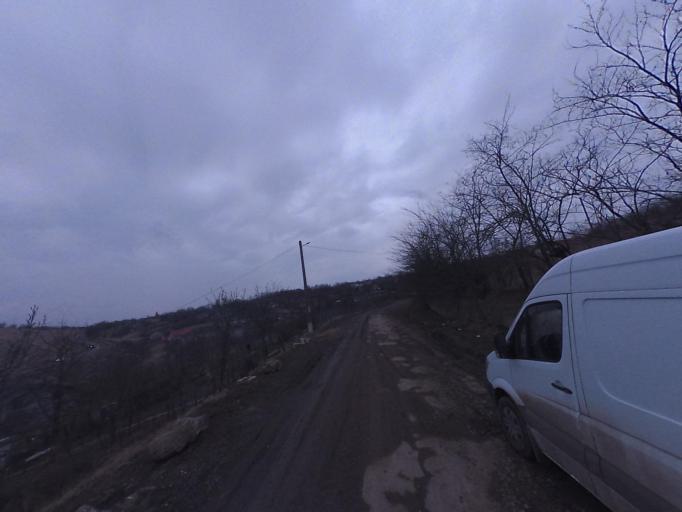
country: RO
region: Iasi
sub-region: Comuna Popricani
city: Popricani
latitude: 47.2968
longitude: 27.5089
